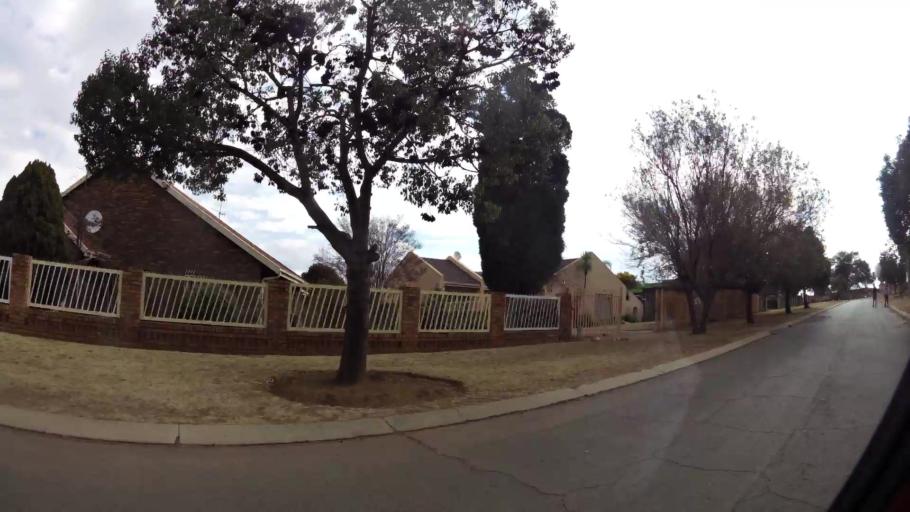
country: ZA
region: Gauteng
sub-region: Sedibeng District Municipality
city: Vanderbijlpark
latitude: -26.7061
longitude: 27.8018
